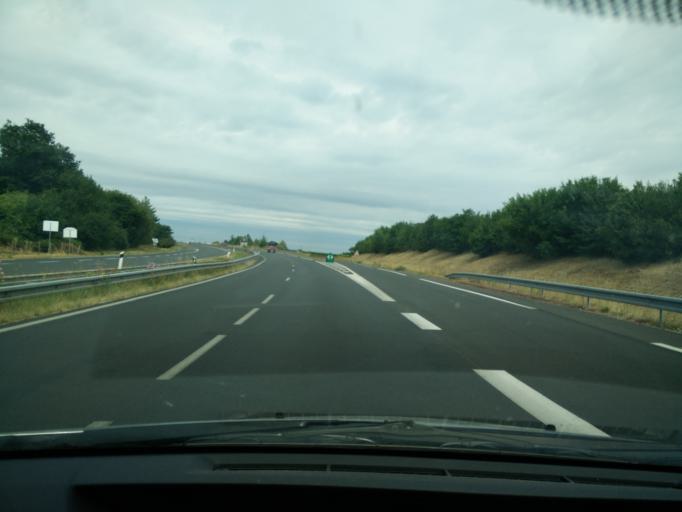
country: FR
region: Pays de la Loire
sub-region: Departement de Maine-et-Loire
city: Brissac-Quince
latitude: 47.3722
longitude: -0.4612
